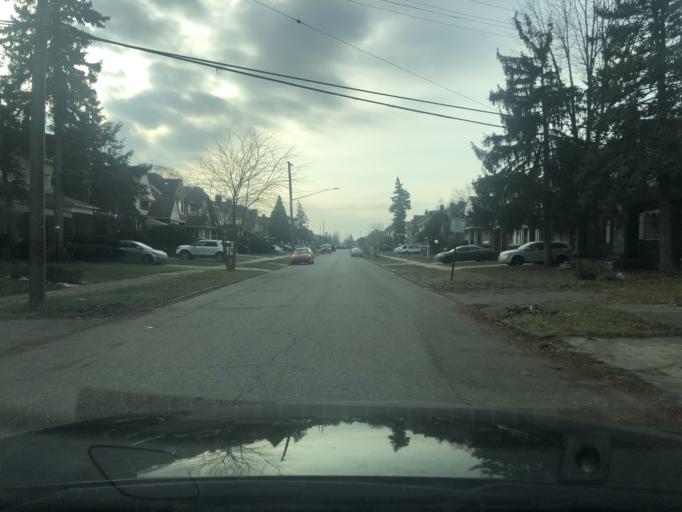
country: US
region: Michigan
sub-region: Wayne County
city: Highland Park
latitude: 42.3887
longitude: -83.1429
